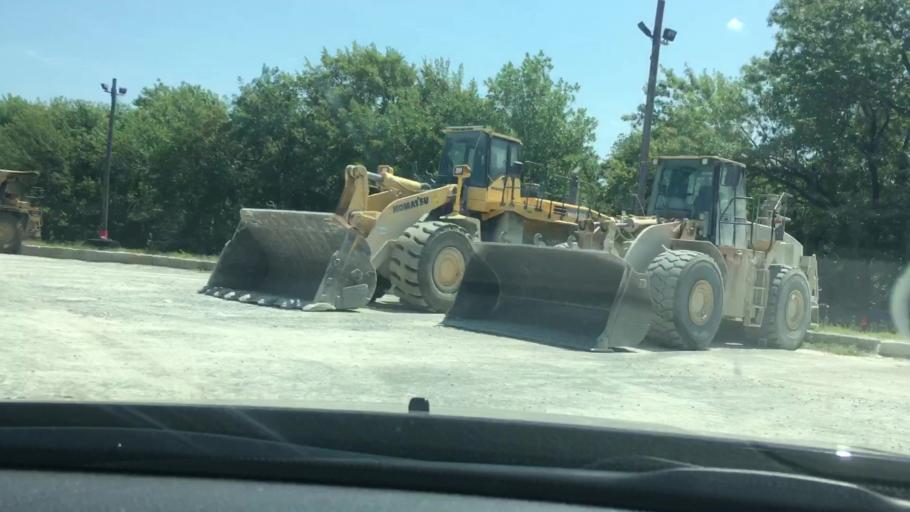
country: US
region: Oklahoma
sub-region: Bryan County
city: Durant
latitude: 34.2575
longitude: -96.3721
